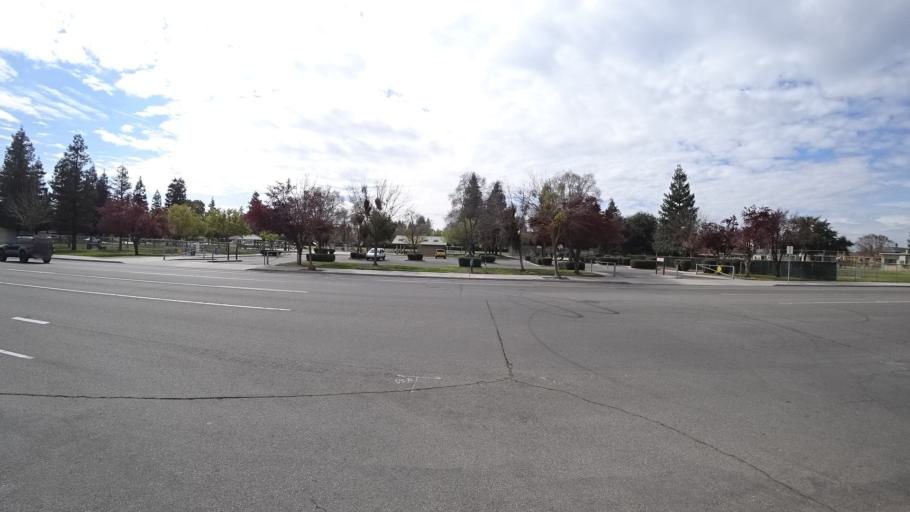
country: US
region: California
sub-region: Fresno County
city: Biola
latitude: 36.8443
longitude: -119.8856
